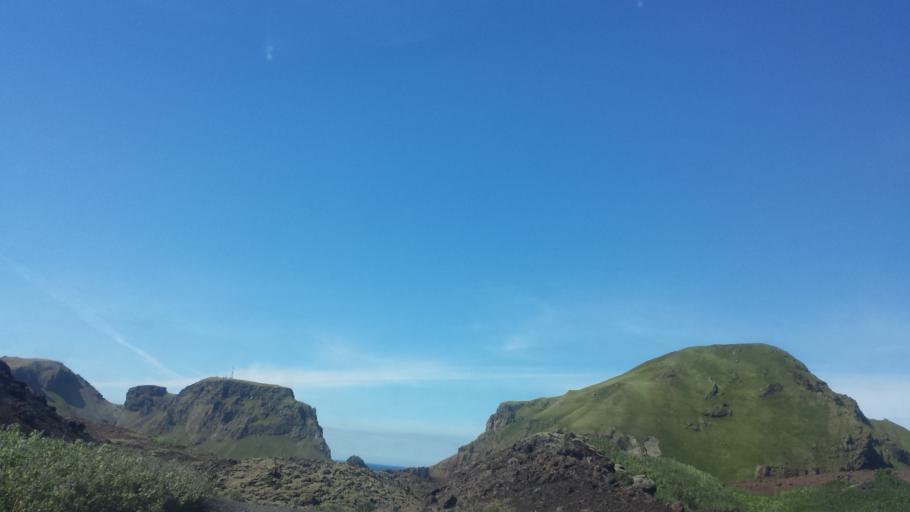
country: IS
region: South
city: Vestmannaeyjar
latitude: 63.4406
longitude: -20.2478
